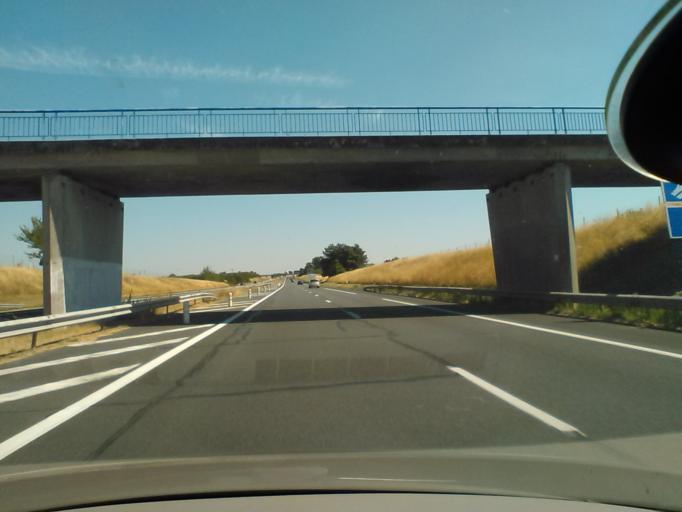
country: FR
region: Ile-de-France
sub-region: Departement de Seine-et-Marne
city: Souppes-sur-Loing
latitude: 48.2137
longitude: 2.7794
